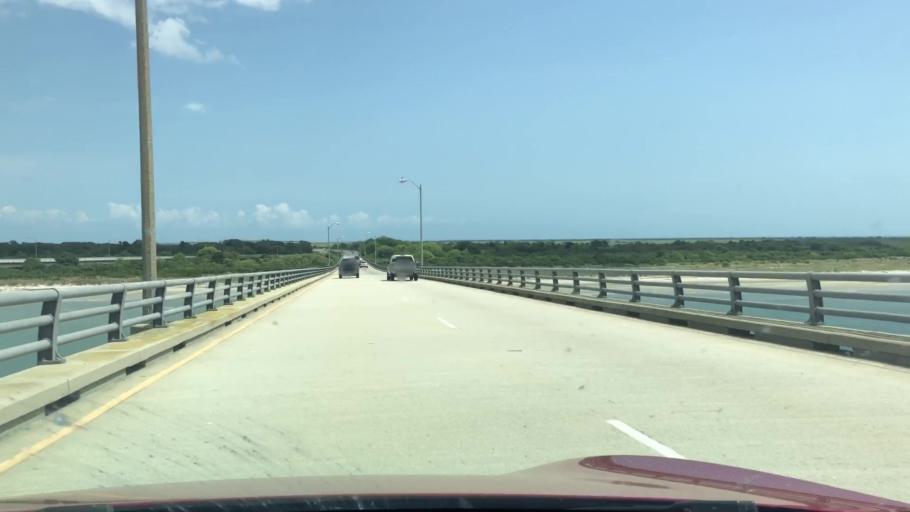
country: US
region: Virginia
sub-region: Northampton County
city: Cape Charles
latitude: 37.0904
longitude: -75.9823
